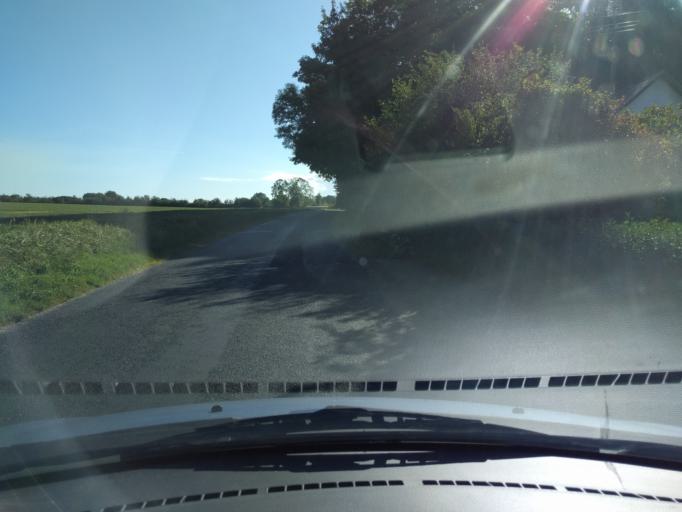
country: DK
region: South Denmark
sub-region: Assens Kommune
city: Harby
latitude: 55.1396
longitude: 10.0187
